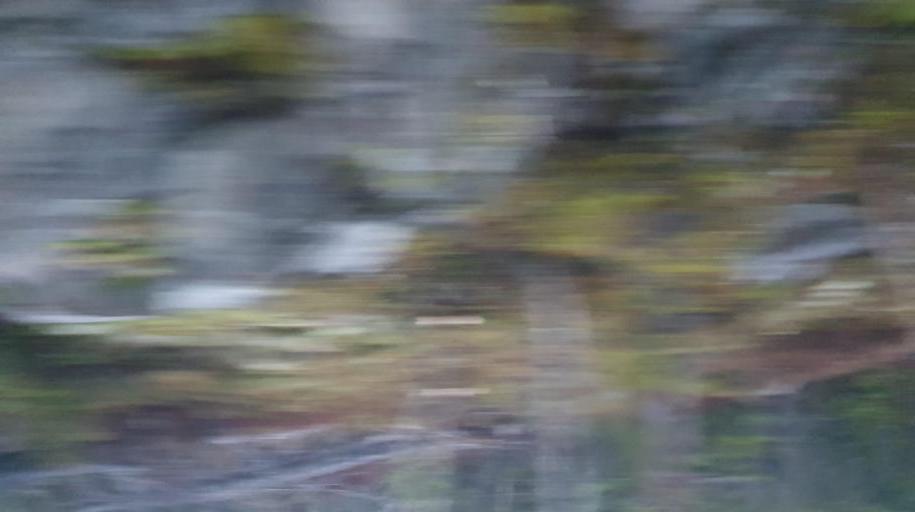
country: NO
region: Buskerud
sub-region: Krodsherad
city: Noresund
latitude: 60.2162
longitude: 9.5435
